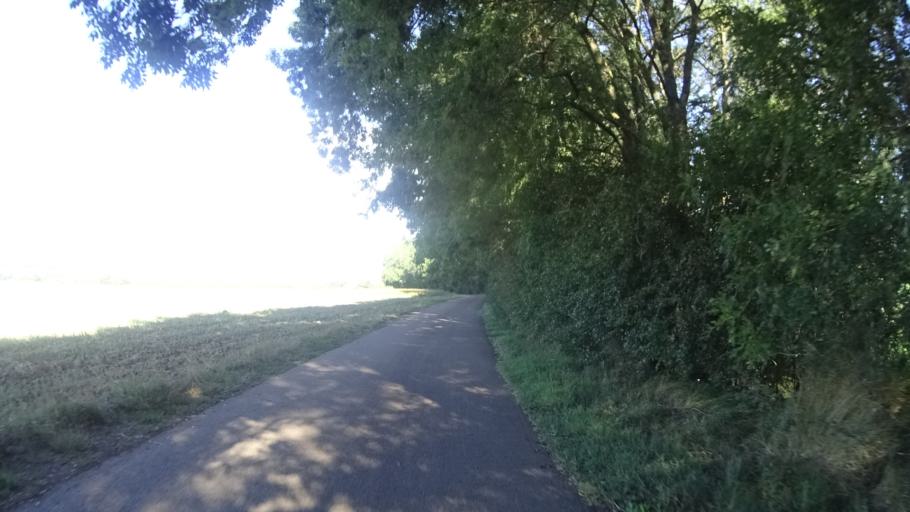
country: FR
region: Bourgogne
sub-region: Departement de la Nievre
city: Pouilly-sur-Loire
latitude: 47.3064
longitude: 2.8988
